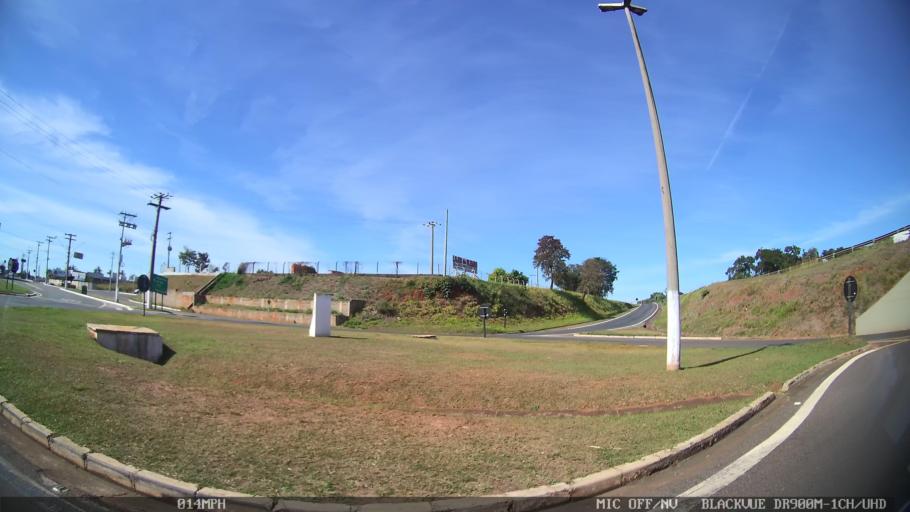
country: BR
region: Sao Paulo
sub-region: Pirassununga
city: Pirassununga
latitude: -22.0129
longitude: -47.4404
